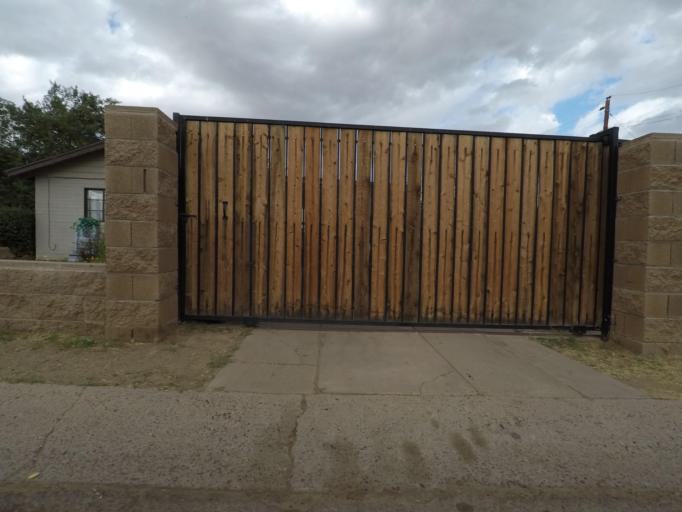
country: US
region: Arizona
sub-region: Maricopa County
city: Phoenix
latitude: 33.4958
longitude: -112.1220
